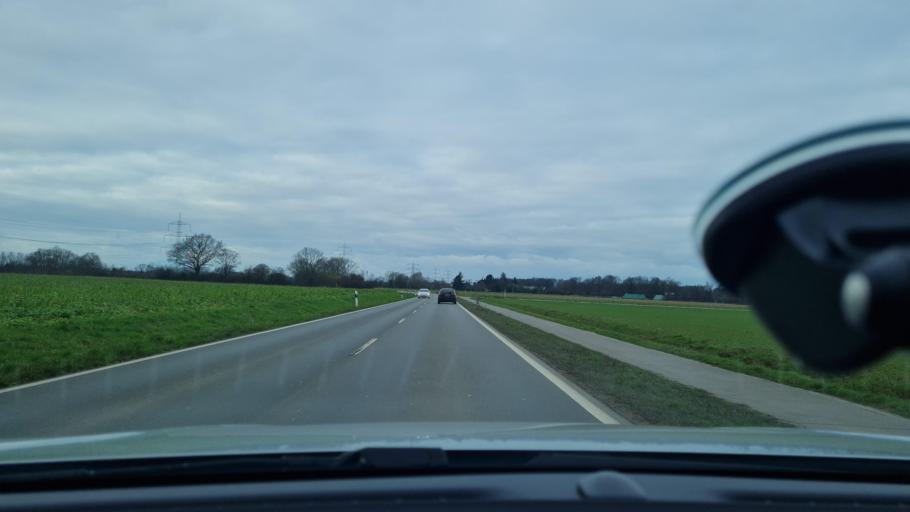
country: DE
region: North Rhine-Westphalia
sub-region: Regierungsbezirk Dusseldorf
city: Voerde
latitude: 51.5844
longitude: 6.6779
